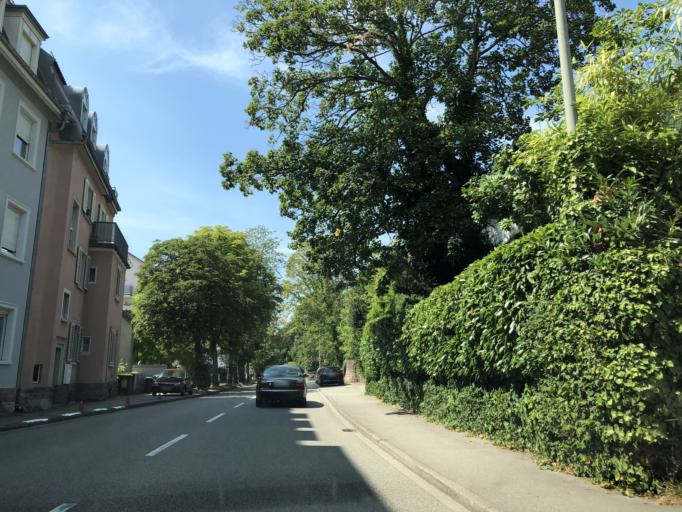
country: DE
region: Baden-Wuerttemberg
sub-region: Karlsruhe Region
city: Baden-Baden
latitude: 48.7505
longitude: 8.2522
